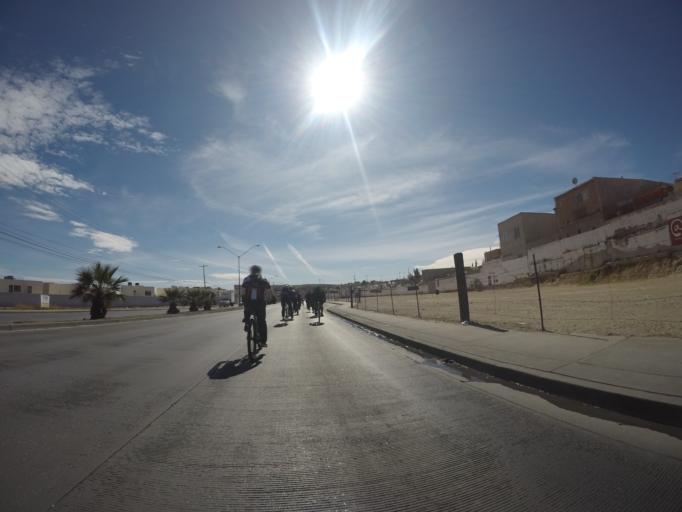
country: MX
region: Chihuahua
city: Ciudad Juarez
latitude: 31.6738
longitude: -106.4053
